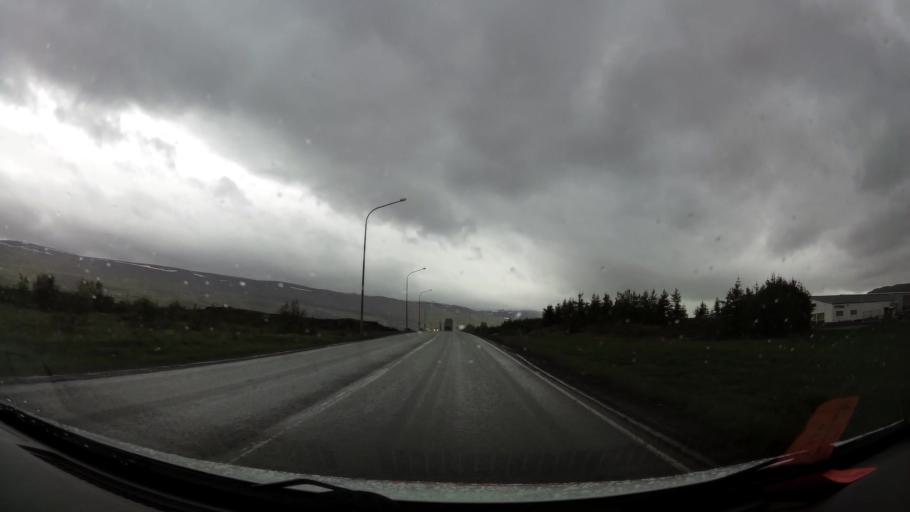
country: IS
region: Northeast
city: Akureyri
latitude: 65.7009
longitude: -18.1458
